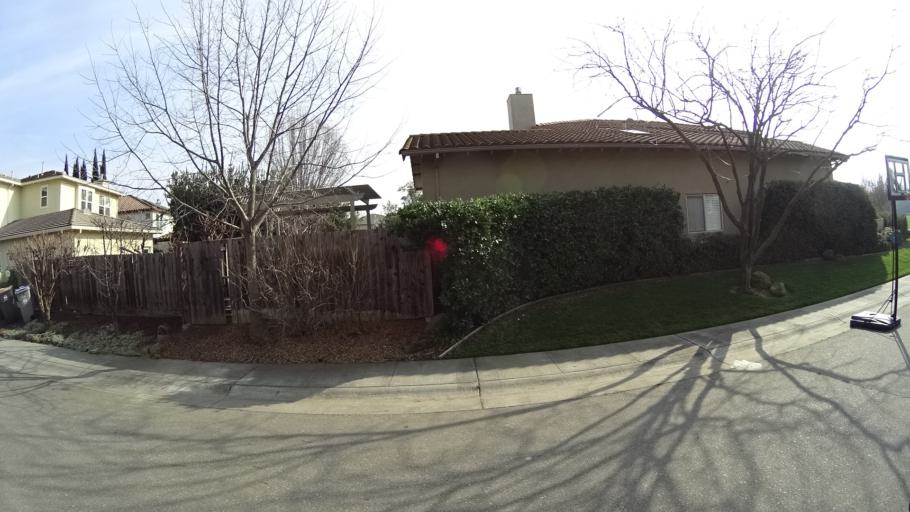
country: US
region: California
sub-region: Yolo County
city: Davis
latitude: 38.5552
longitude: -121.7721
